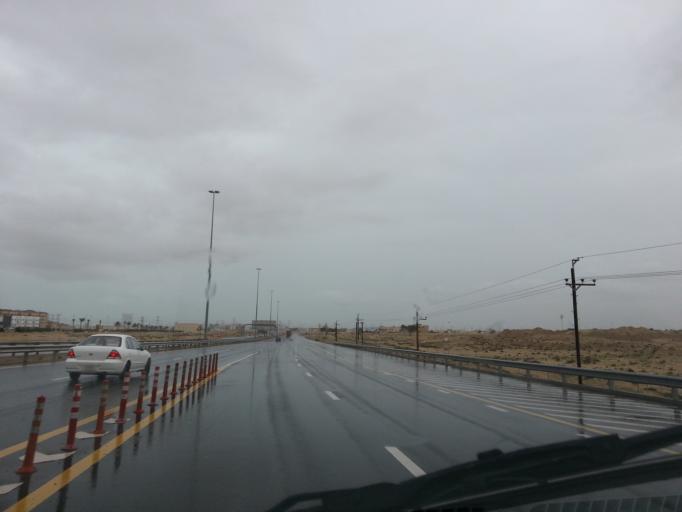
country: AE
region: Dubai
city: Dubai
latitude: 25.0575
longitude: 55.2222
